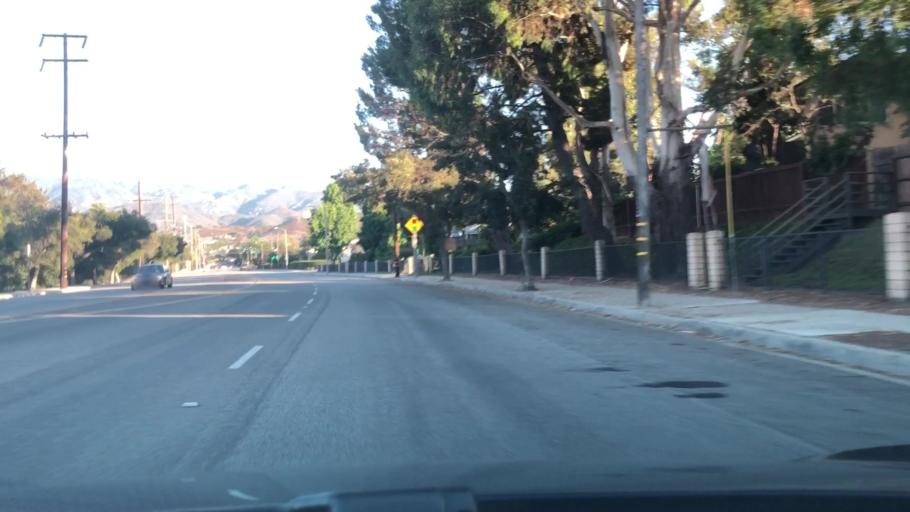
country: US
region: California
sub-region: Ventura County
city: Casa Conejo
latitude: 34.1846
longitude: -118.9541
